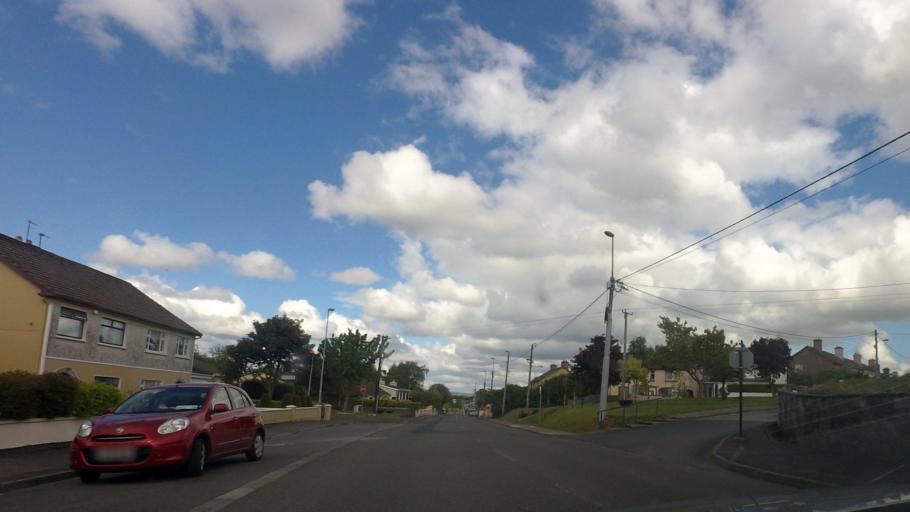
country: IE
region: Munster
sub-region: An Clar
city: Ennis
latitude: 52.8444
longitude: -8.9961
